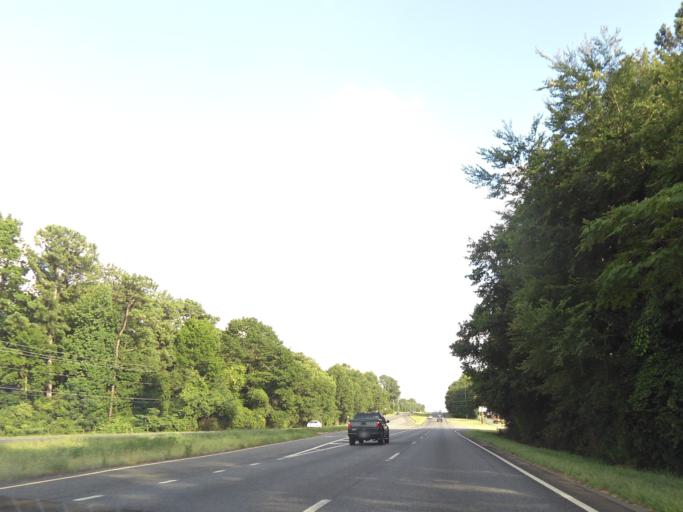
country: US
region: Georgia
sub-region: Houston County
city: Centerville
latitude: 32.7104
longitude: -83.6459
